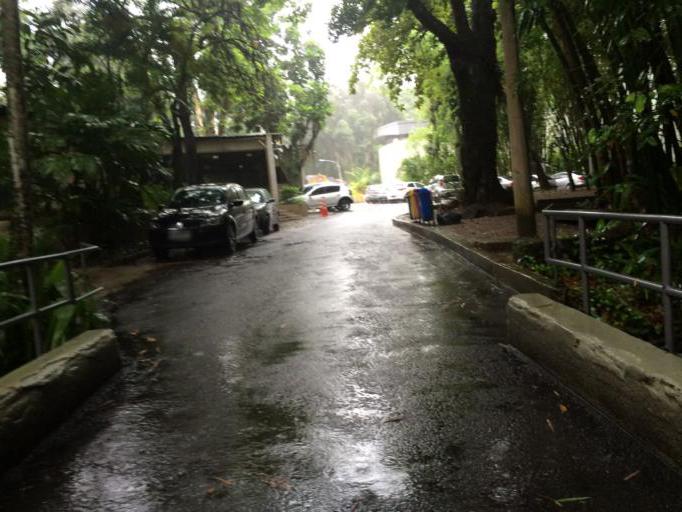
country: BR
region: Rio de Janeiro
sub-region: Rio De Janeiro
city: Rio de Janeiro
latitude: -22.9802
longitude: -43.2335
